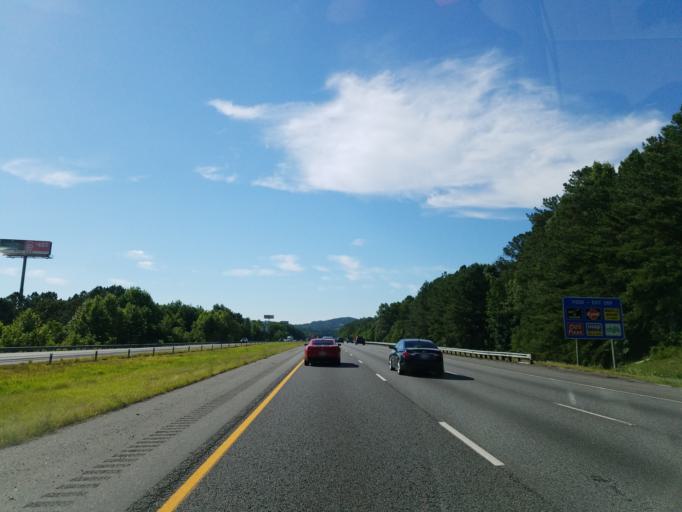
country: US
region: Georgia
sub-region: Bartow County
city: Emerson
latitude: 34.1487
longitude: -84.7440
